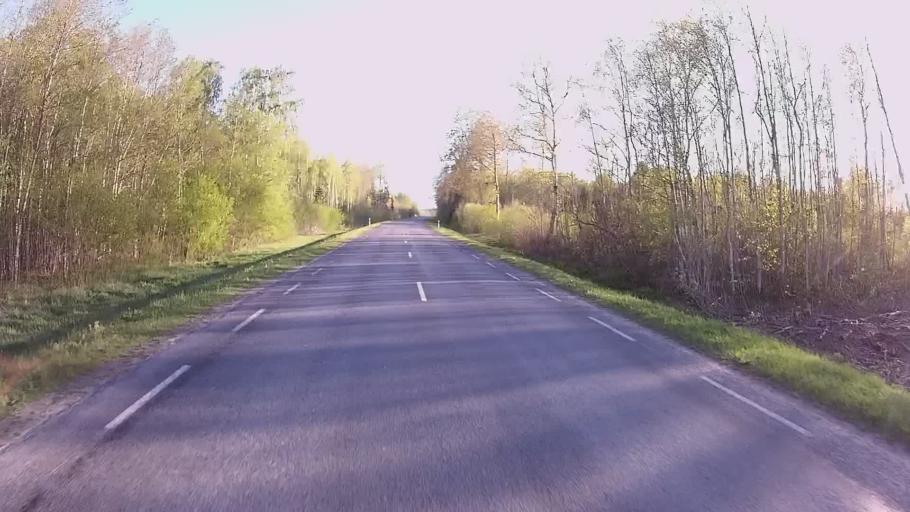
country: EE
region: Viljandimaa
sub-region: Viiratsi vald
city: Viiratsi
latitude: 58.4310
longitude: 25.7186
